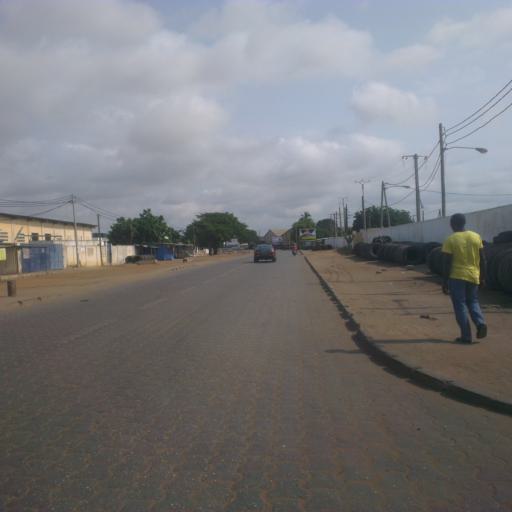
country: TG
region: Maritime
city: Lome
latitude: 6.1460
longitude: 1.2739
